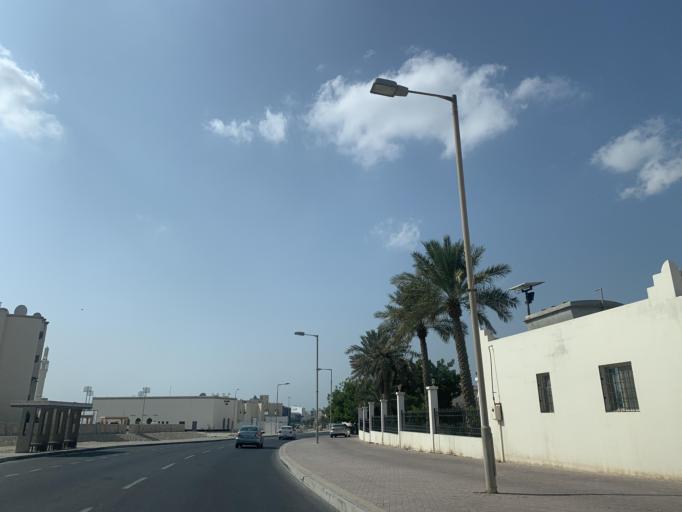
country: BH
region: Central Governorate
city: Madinat Hamad
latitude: 26.1341
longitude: 50.5010
